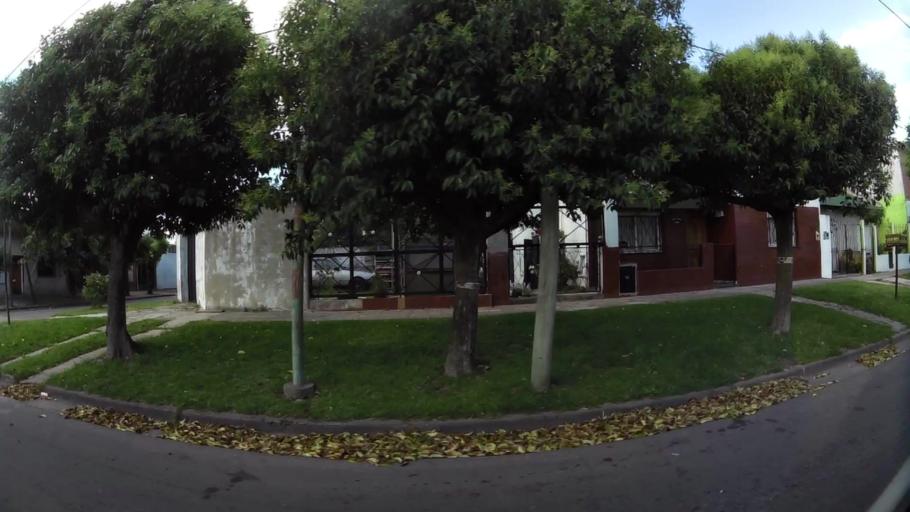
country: AR
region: Buenos Aires
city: San Justo
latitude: -34.6727
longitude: -58.5778
